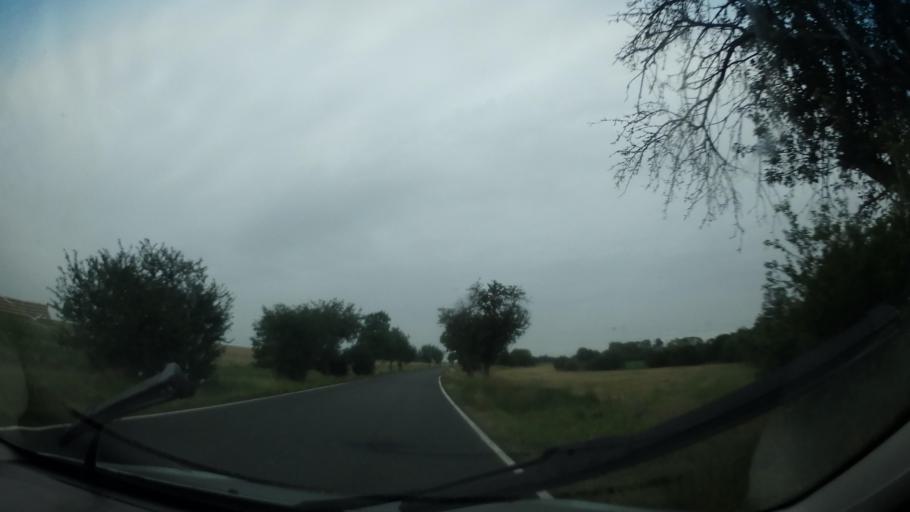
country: CZ
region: Central Bohemia
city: Loucen
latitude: 50.2383
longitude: 15.0131
